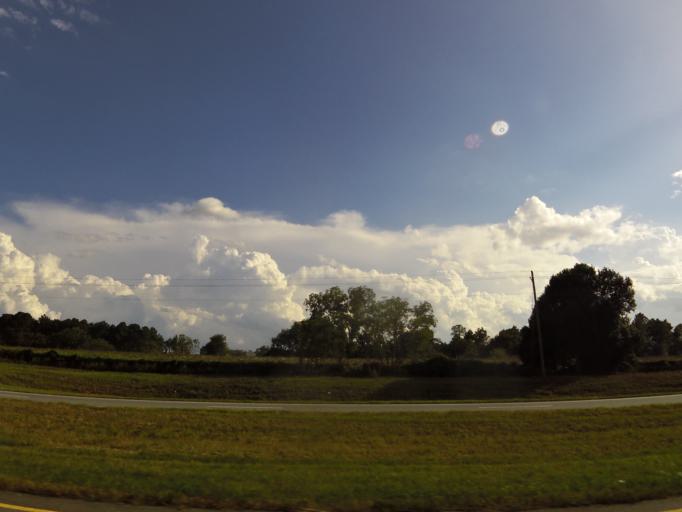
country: US
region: Georgia
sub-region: Brooks County
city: Quitman
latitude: 30.7849
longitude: -83.6204
